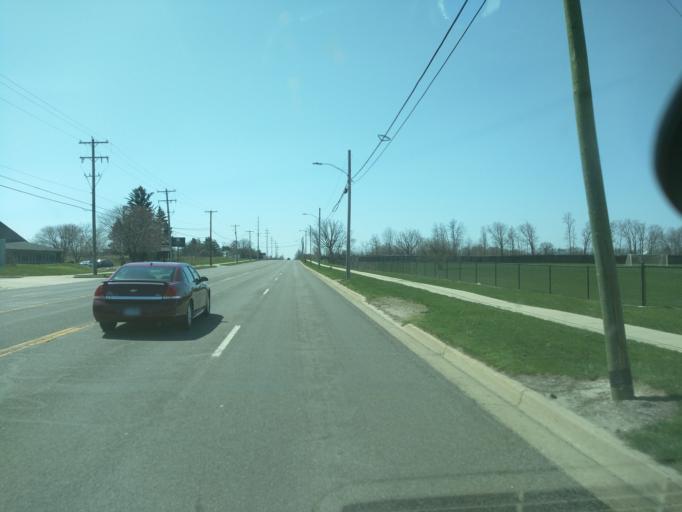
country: US
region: Michigan
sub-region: Kent County
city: East Grand Rapids
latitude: 42.9332
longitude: -85.5701
